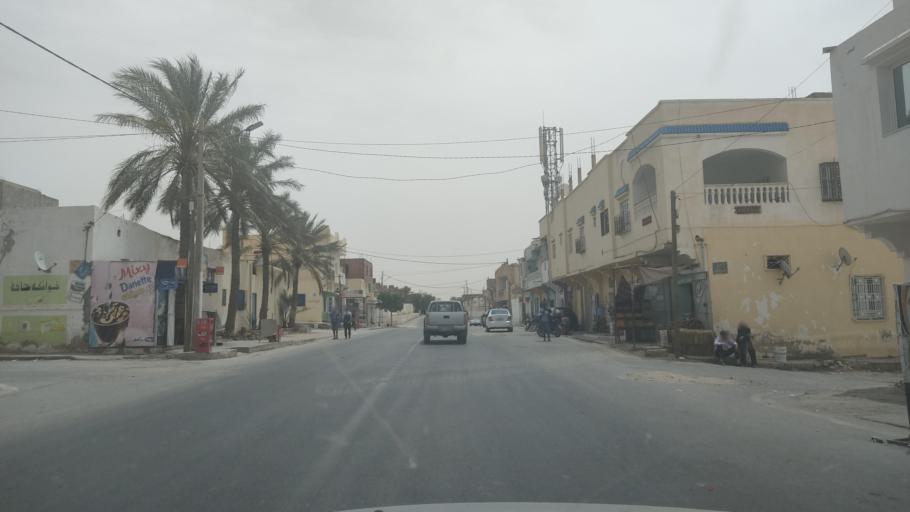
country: TN
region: Gafsa
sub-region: Gafsa Municipality
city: Gafsa
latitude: 34.3391
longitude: 8.9516
